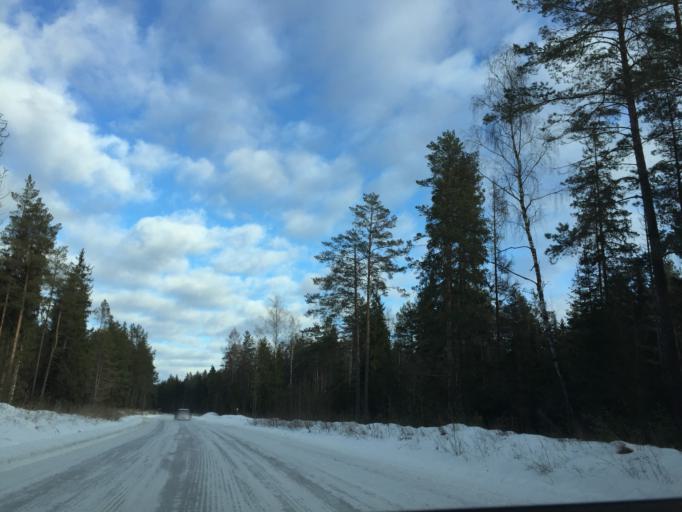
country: LV
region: Ogre
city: Jumprava
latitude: 56.5695
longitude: 24.9330
